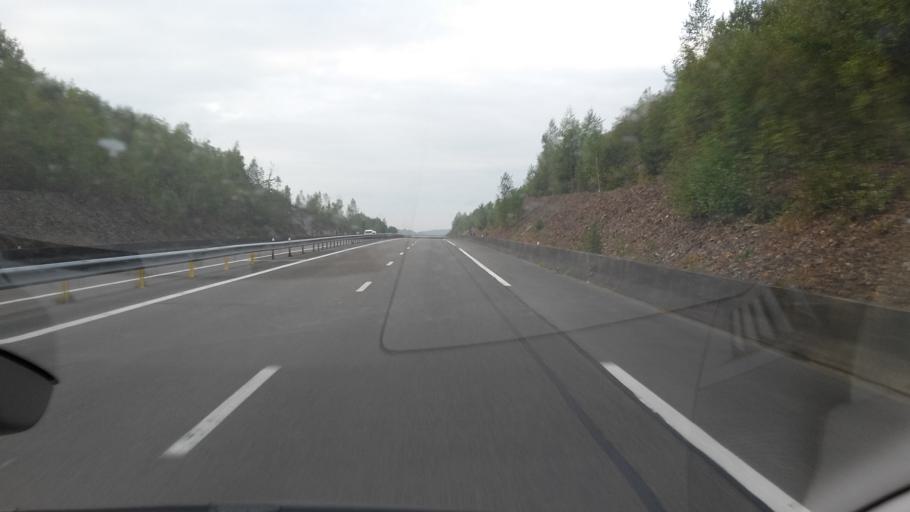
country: FR
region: Champagne-Ardenne
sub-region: Departement des Ardennes
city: Attigny
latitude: 49.6305
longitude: 4.5574
